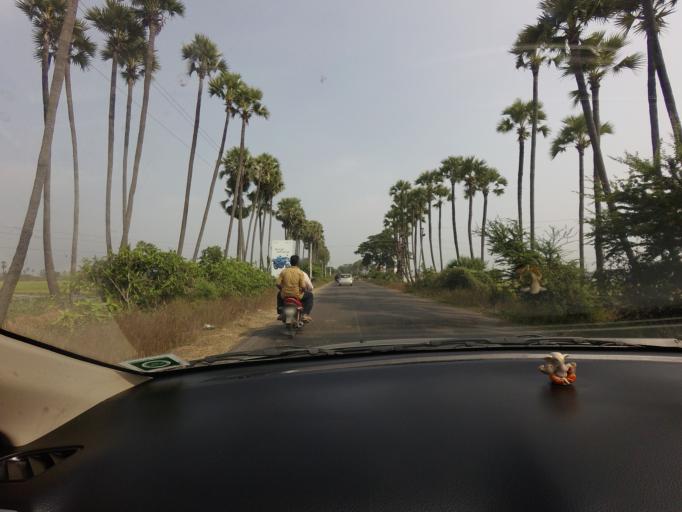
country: IN
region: Andhra Pradesh
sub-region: Krishna
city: Kankipadu
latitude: 16.4542
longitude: 80.7913
